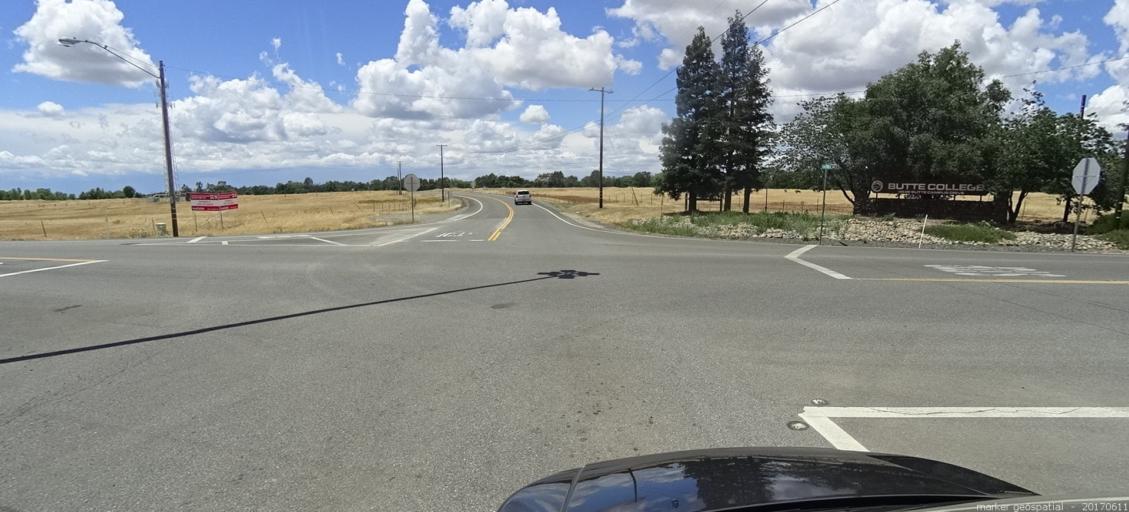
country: US
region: California
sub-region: Butte County
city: Paradise
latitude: 39.6473
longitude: -121.6343
